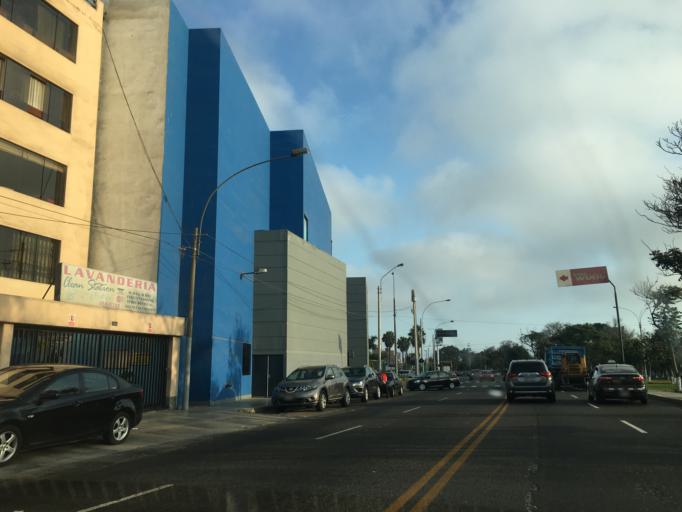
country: PE
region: Callao
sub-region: Callao
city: Callao
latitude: -12.0754
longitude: -77.0841
